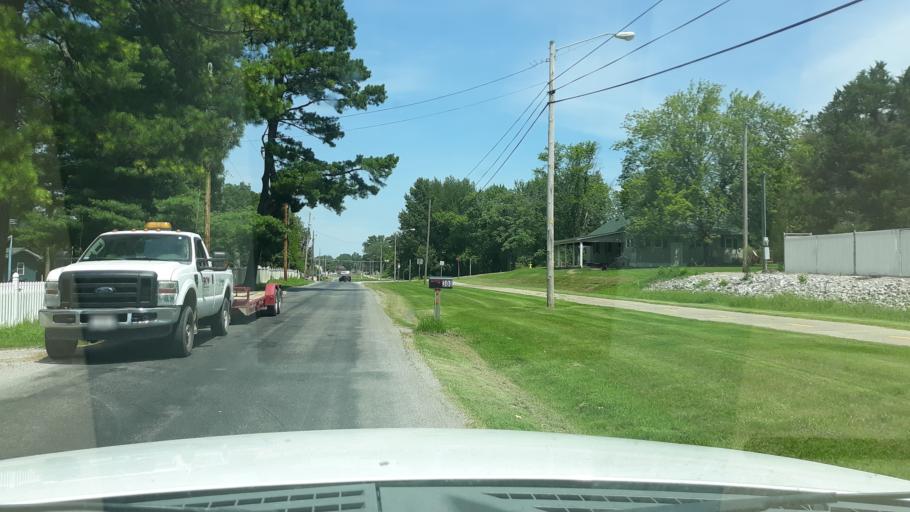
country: US
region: Illinois
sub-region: Saline County
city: Eldorado
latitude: 37.8049
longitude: -88.4328
